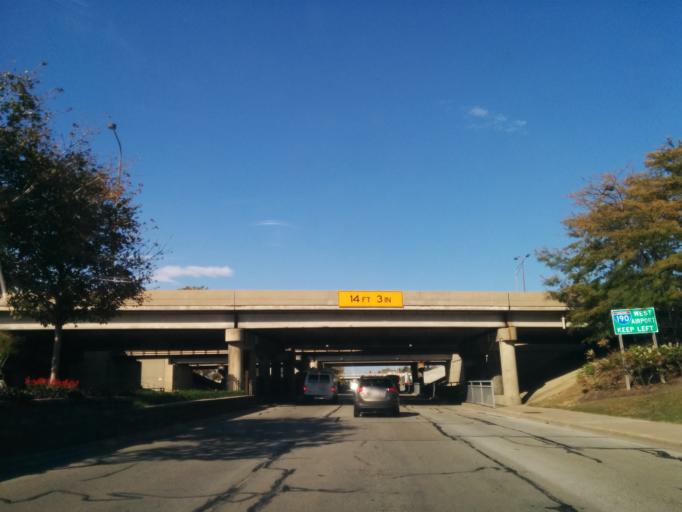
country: US
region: Illinois
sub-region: Cook County
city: Rosemont
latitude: 41.9829
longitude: -87.8616
